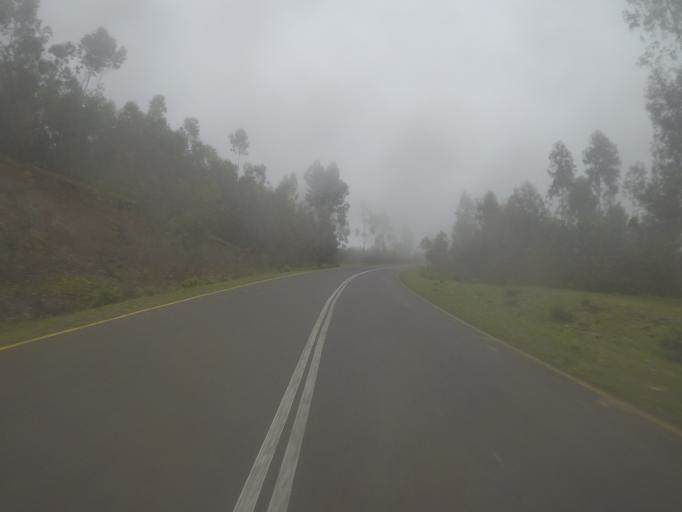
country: ET
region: Amhara
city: Gondar
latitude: 12.7522
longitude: 37.5354
